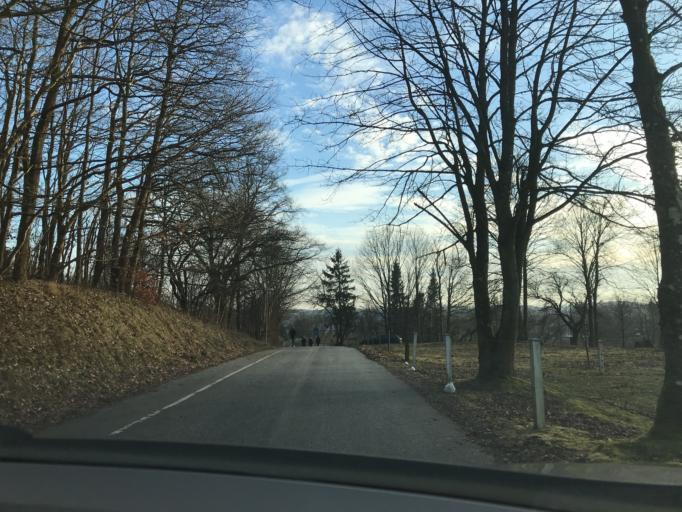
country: DK
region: South Denmark
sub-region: Vejle Kommune
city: Vejle
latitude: 55.6886
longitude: 9.5312
